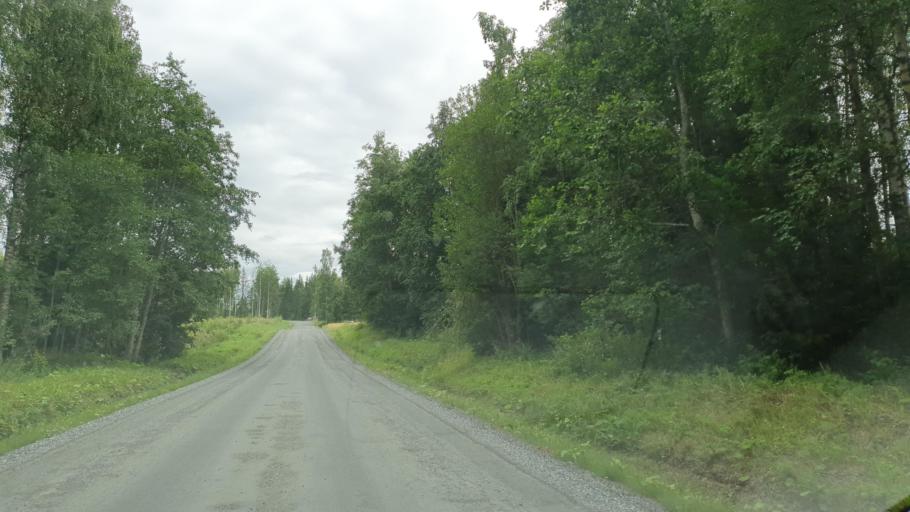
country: FI
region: Northern Savo
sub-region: Ylae-Savo
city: Iisalmi
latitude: 63.5210
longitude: 27.0976
